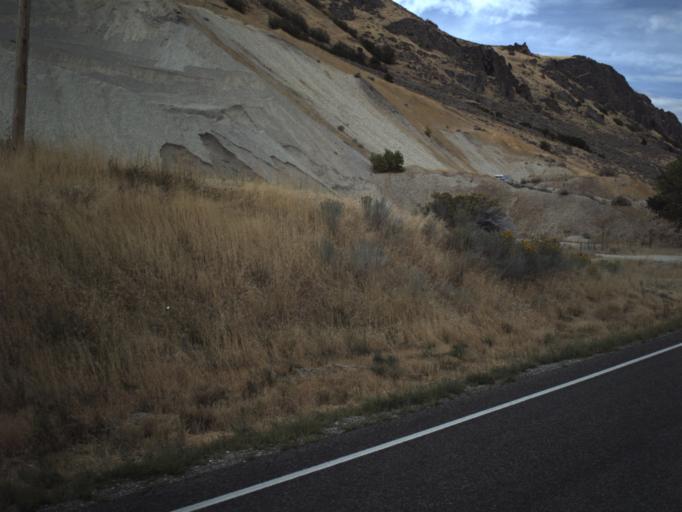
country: US
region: Utah
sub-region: Cache County
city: Benson
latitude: 41.8941
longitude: -111.9492
